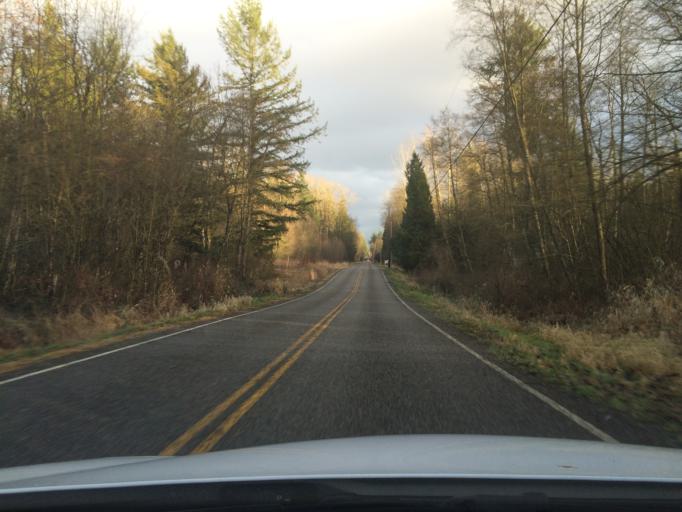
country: CA
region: British Columbia
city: Langley
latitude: 48.9935
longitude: -122.6049
